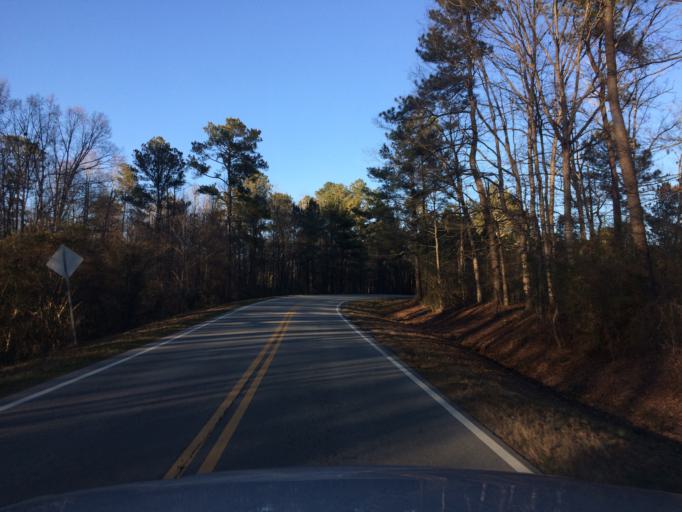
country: US
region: Georgia
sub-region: Barrow County
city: Winder
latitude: 33.9759
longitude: -83.7679
